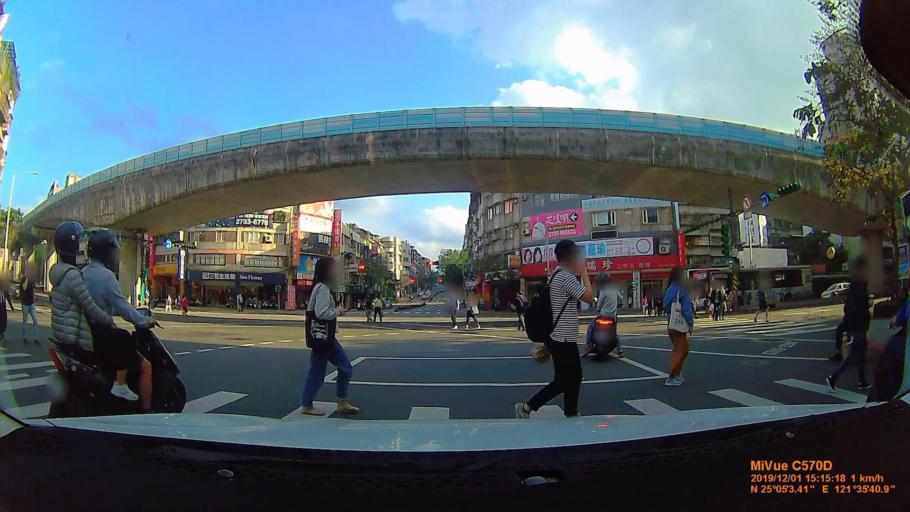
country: TW
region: Taipei
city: Taipei
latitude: 25.0843
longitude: 121.5948
